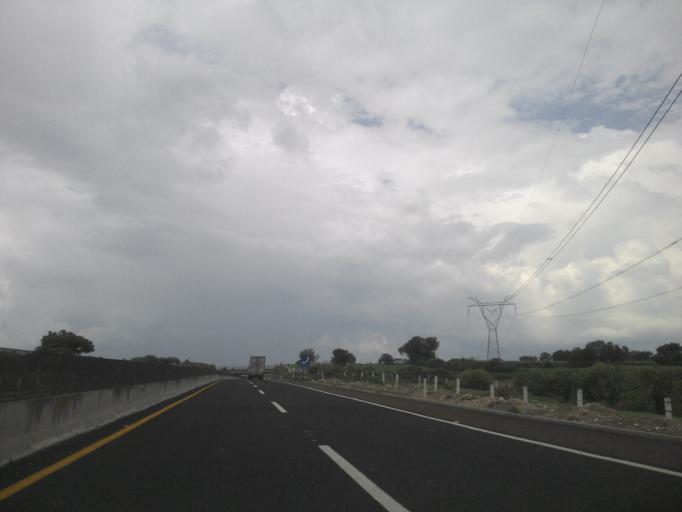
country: MX
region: Hidalgo
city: San Marcos
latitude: 20.0807
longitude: -99.3402
